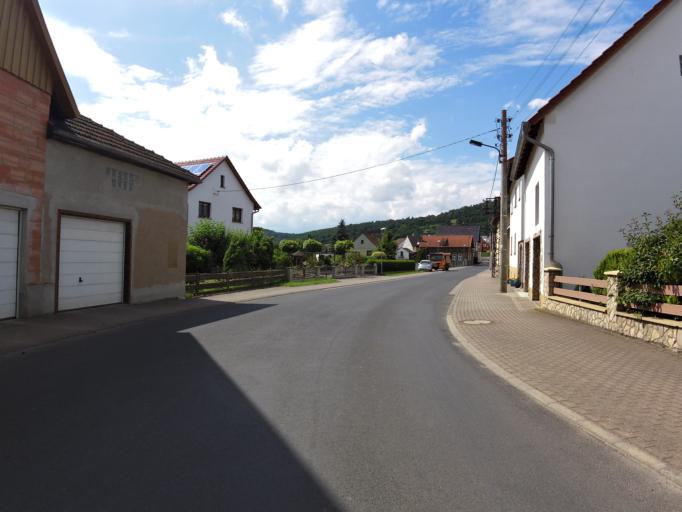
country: DE
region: Thuringia
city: Dorndorf
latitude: 50.8405
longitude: 10.1168
